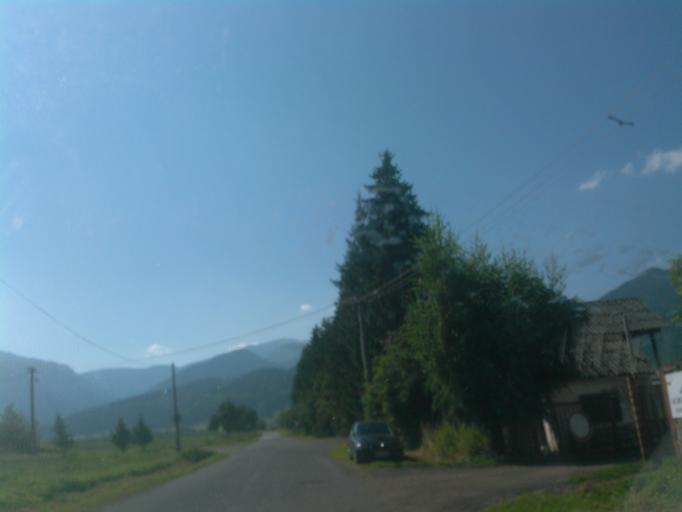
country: SK
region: Zilinsky
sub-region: Okres Liptovsky Mikulas
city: Liptovsky Mikulas
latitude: 49.0320
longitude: 19.5041
